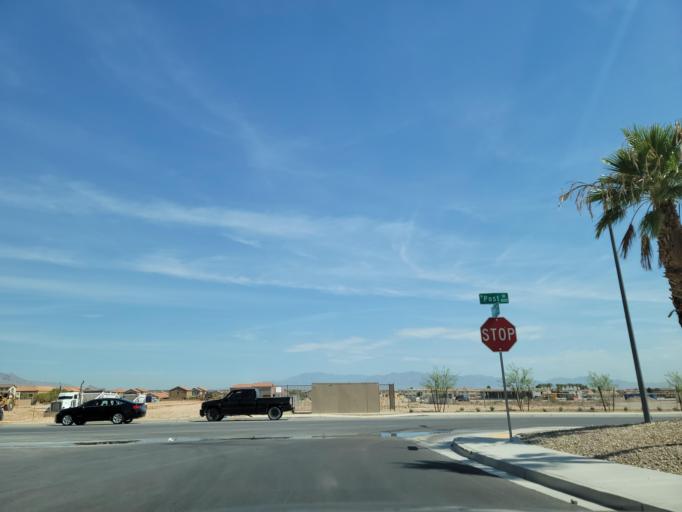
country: US
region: Nevada
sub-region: Clark County
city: Spring Valley
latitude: 36.0736
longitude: -115.2654
